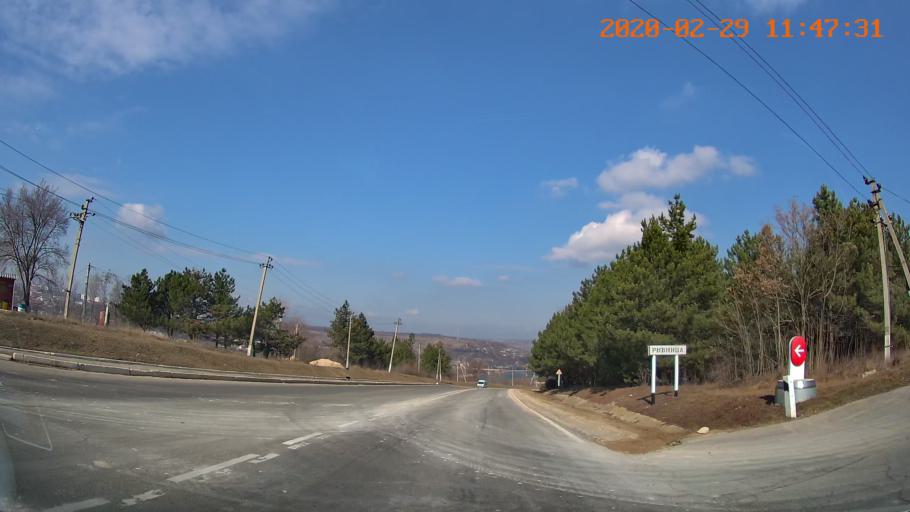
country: MD
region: Rezina
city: Rezina
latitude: 47.7420
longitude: 28.9877
